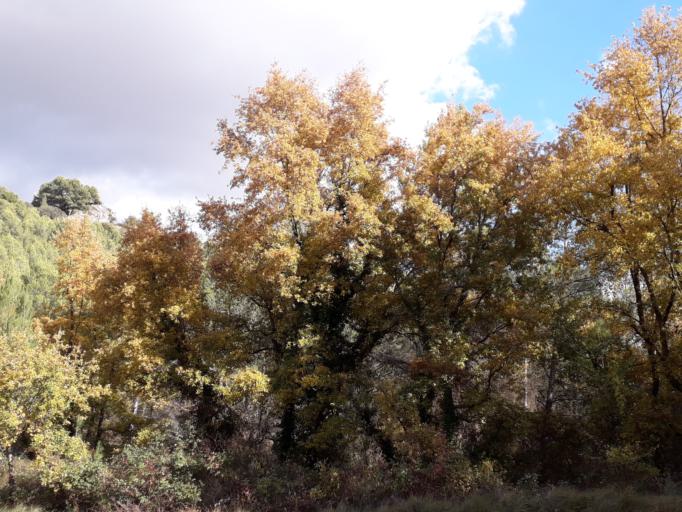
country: ES
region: Catalonia
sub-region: Provincia de Barcelona
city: Sant Marti de Tous
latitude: 41.5170
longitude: 1.5155
